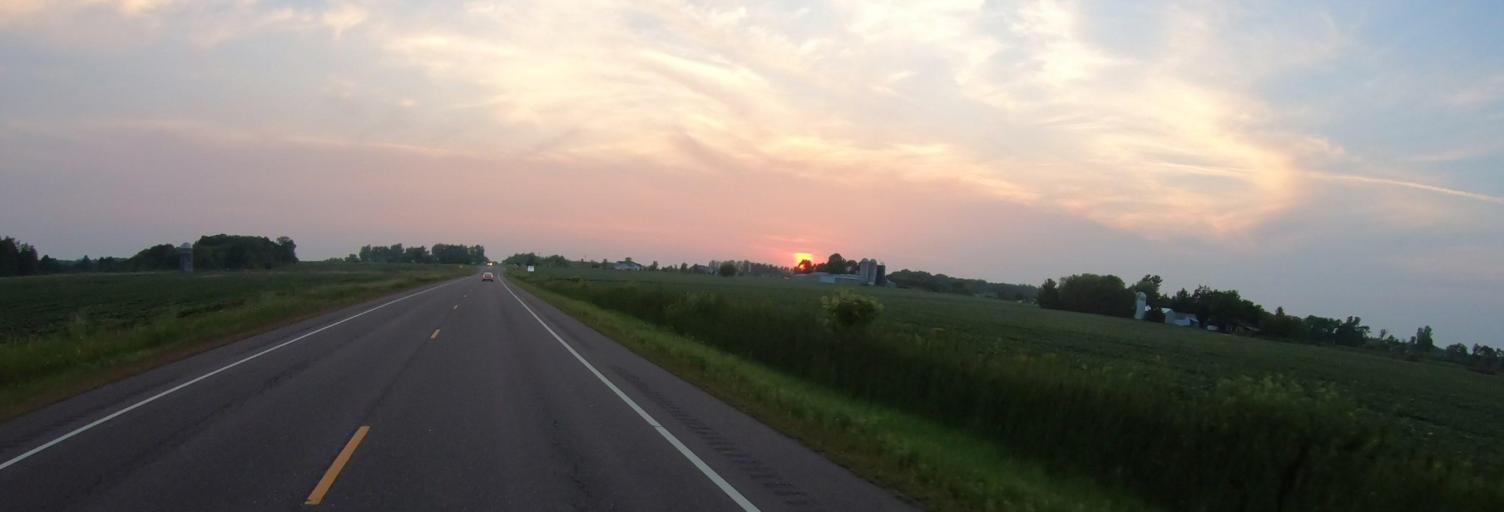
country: US
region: Minnesota
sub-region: Pine County
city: Rock Creek
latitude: 45.7734
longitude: -92.9254
